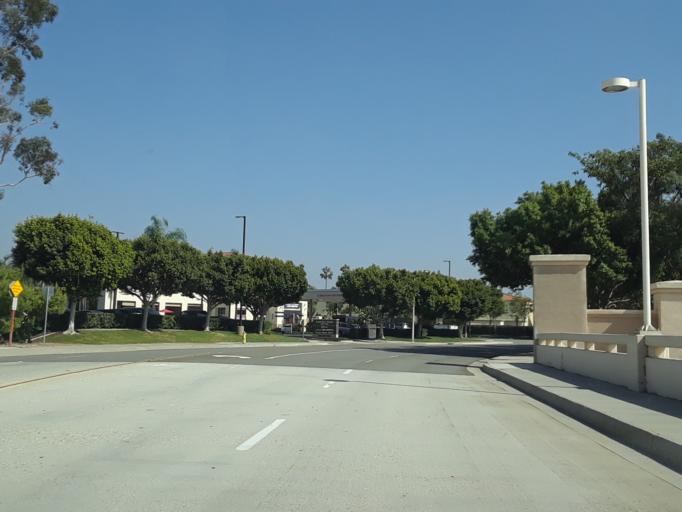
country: US
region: California
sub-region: Orange County
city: Irvine
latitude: 33.6772
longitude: -117.8356
